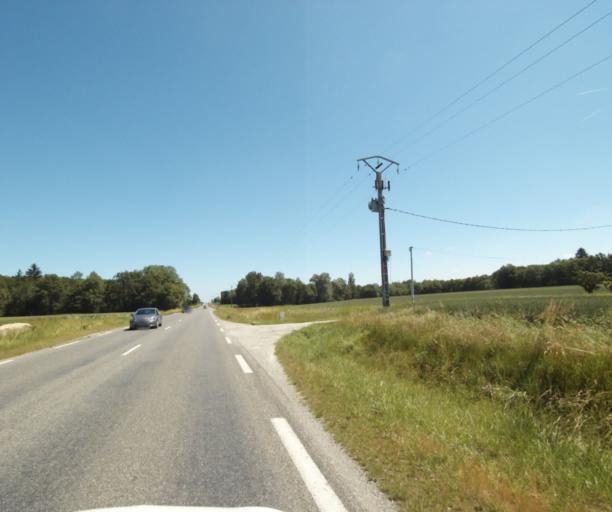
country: FR
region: Rhone-Alpes
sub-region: Departement de la Haute-Savoie
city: Veigy-Foncenex
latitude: 46.2906
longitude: 6.2709
